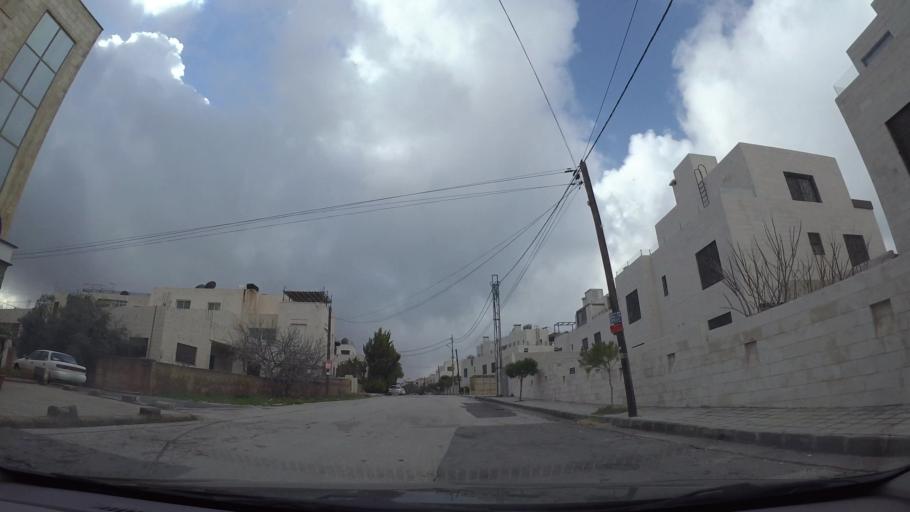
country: JO
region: Amman
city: Amman
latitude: 31.9426
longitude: 35.9035
